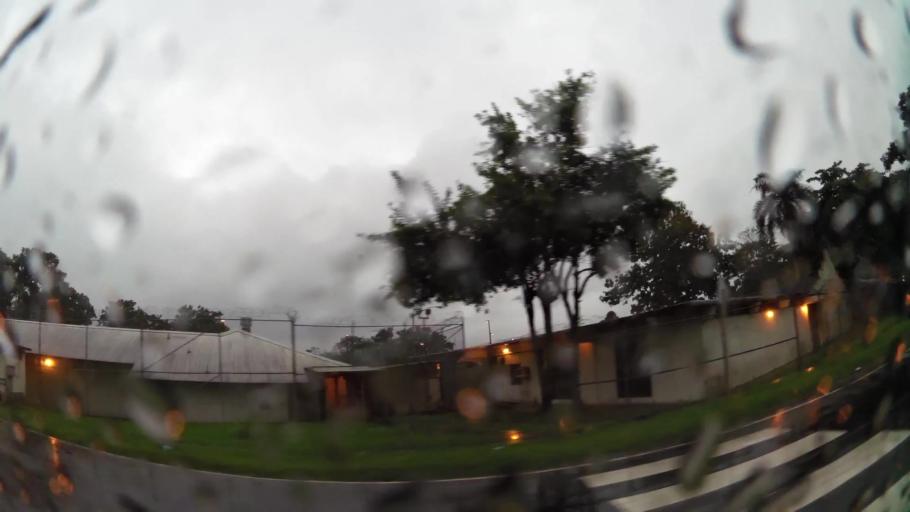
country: PA
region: Panama
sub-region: Distrito de Panama
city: Paraiso
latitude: 9.0248
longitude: -79.6186
